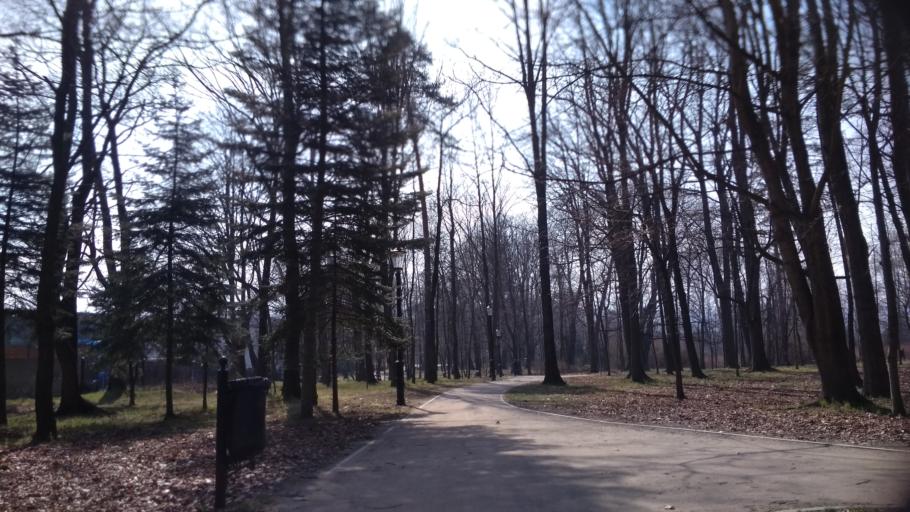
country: PL
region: Lower Silesian Voivodeship
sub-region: Jelenia Gora
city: Cieplice Slaskie Zdroj
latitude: 50.8622
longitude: 15.6838
